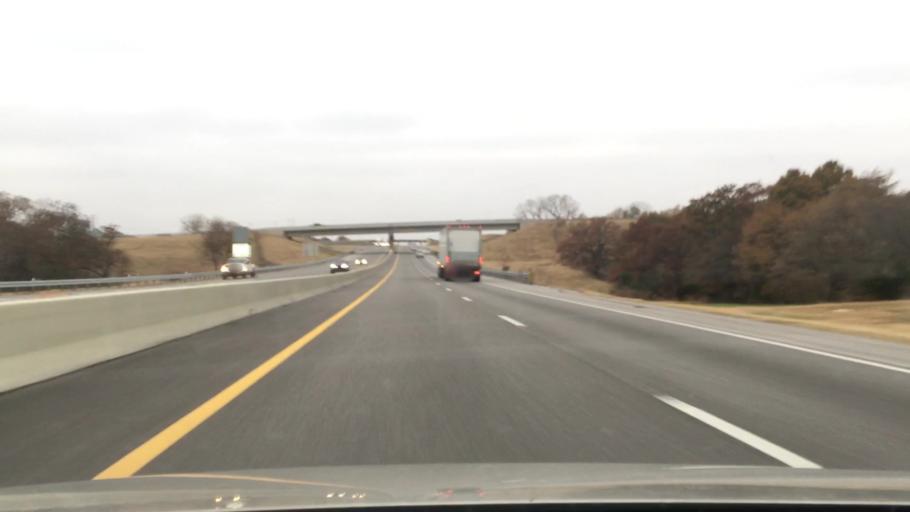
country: US
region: Oklahoma
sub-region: Lincoln County
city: Chandler
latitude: 35.7197
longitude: -96.8815
